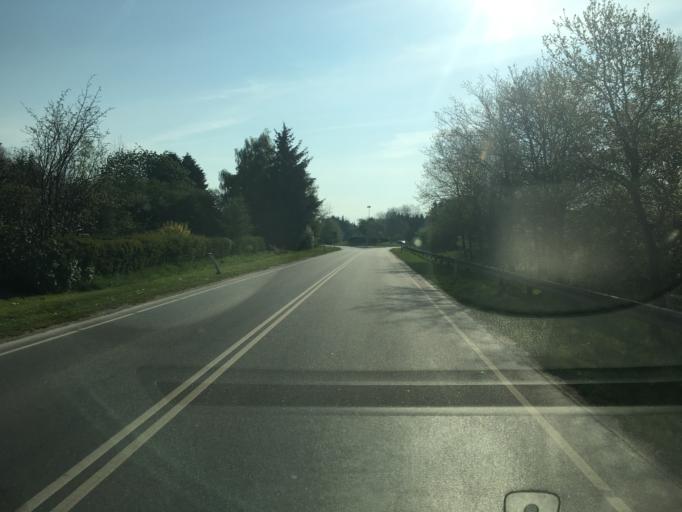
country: DK
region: South Denmark
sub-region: Aabenraa Kommune
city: Aabenraa
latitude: 55.0817
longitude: 9.3807
